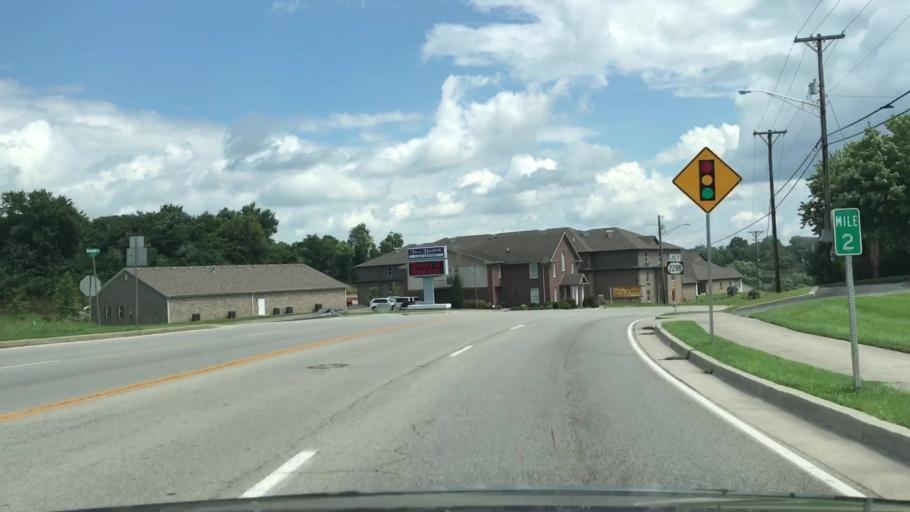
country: US
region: Kentucky
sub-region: Pulaski County
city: Somerset
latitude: 37.0772
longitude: -84.6144
